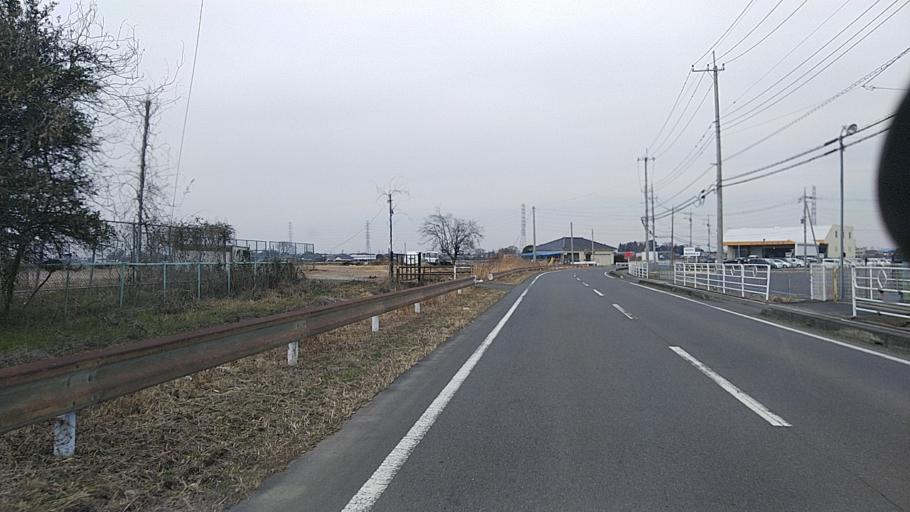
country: JP
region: Ibaraki
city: Ishige
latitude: 36.1656
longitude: 139.9904
